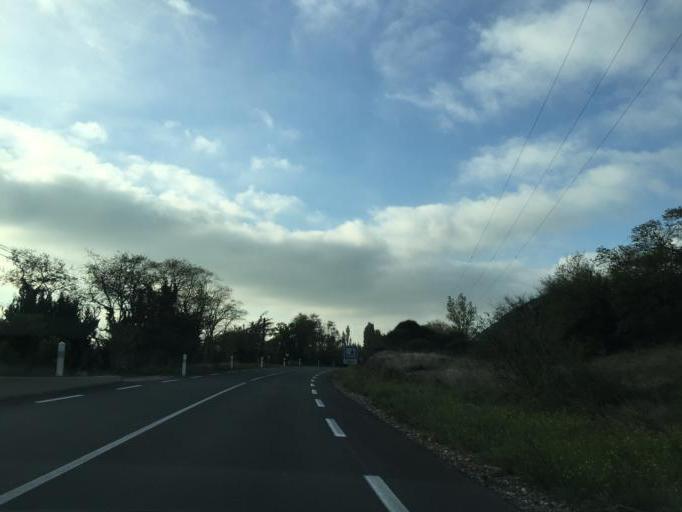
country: FR
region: Rhone-Alpes
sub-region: Departement de l'Ardeche
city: Viviers
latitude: 44.4631
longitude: 4.6890
